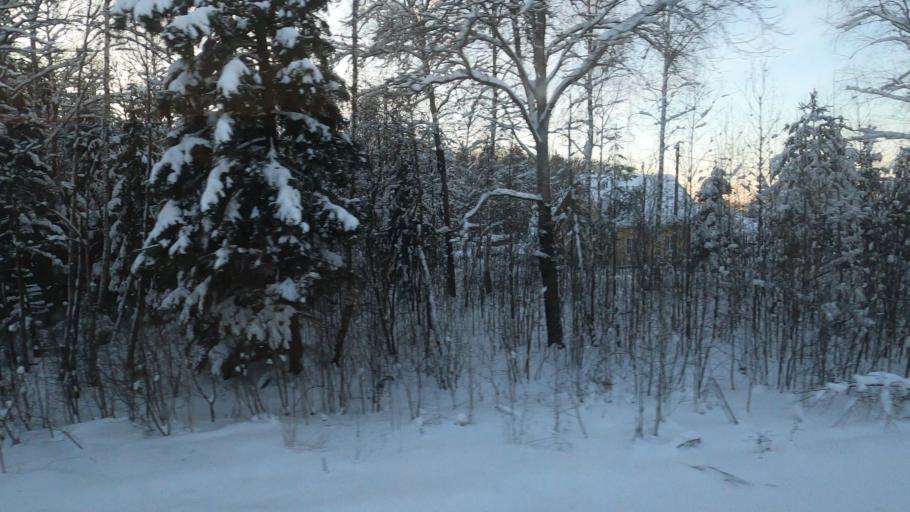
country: RU
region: Moskovskaya
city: Novo-Nikol'skoye
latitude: 56.5831
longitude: 37.5672
